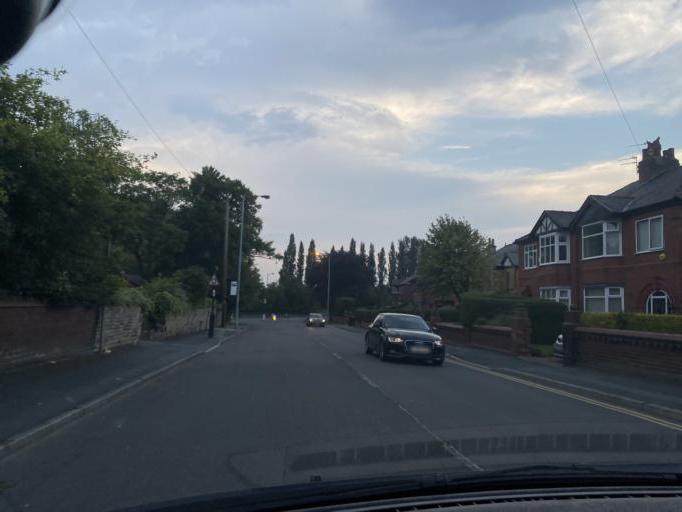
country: GB
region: England
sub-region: Borough of Tameside
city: Denton
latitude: 53.4713
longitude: -2.1236
